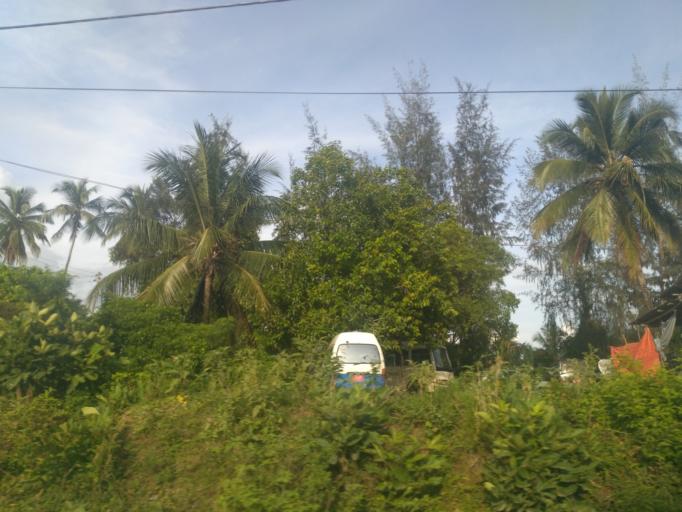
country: TZ
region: Zanzibar Urban/West
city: Zanzibar
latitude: -6.1496
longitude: 39.2362
